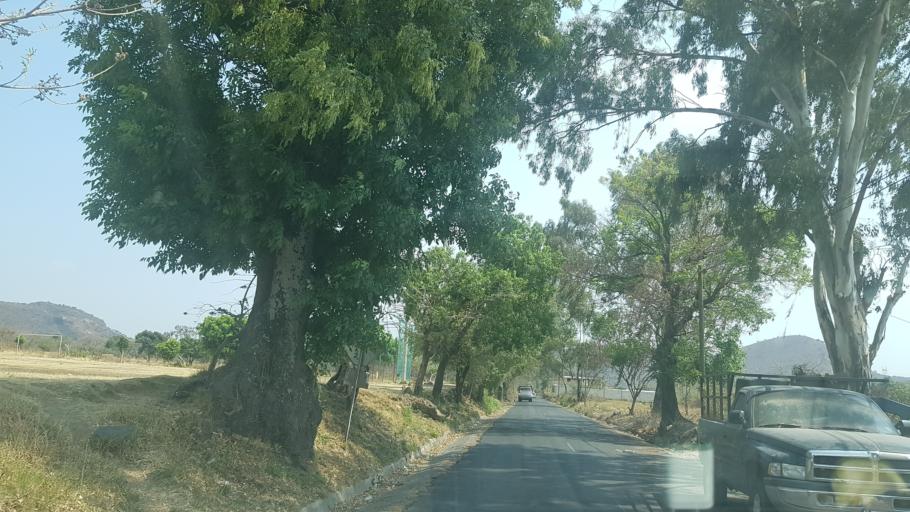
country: MX
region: Puebla
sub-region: Tianguismanalco
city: San Martin Tlapala
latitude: 18.9599
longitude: -98.4591
